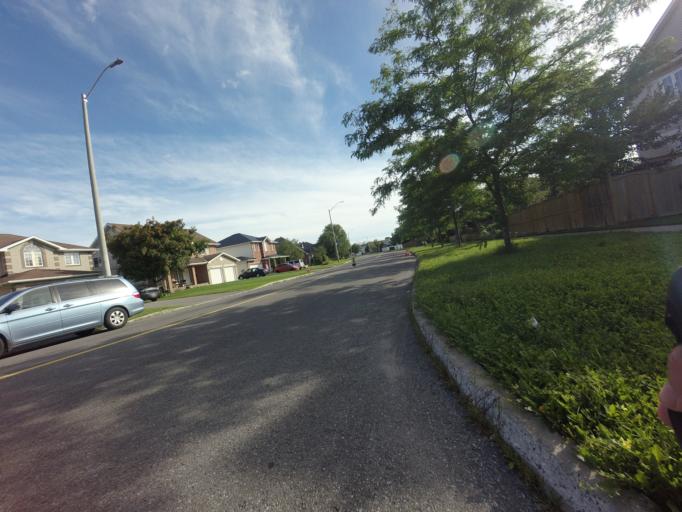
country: CA
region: Ontario
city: Ottawa
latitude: 45.2875
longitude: -75.6876
